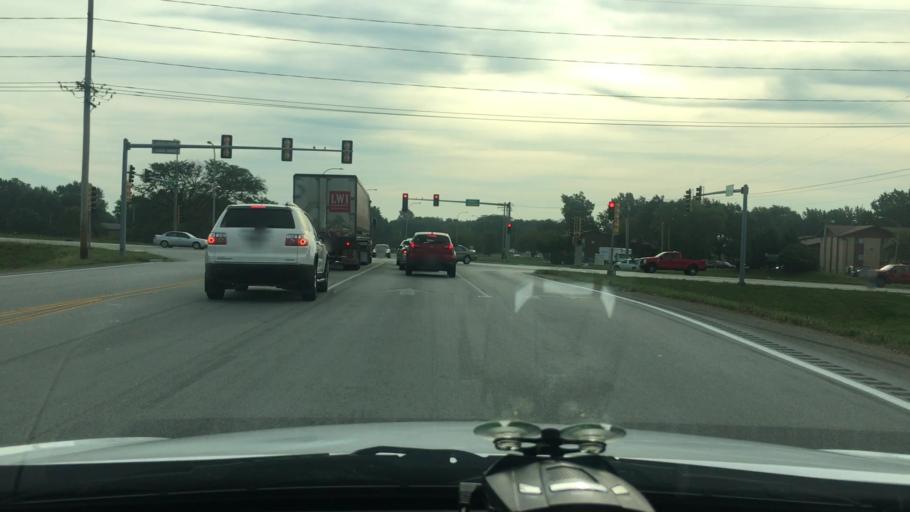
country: US
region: Illinois
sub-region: Champaign County
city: Champaign
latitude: 40.1391
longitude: -88.2781
